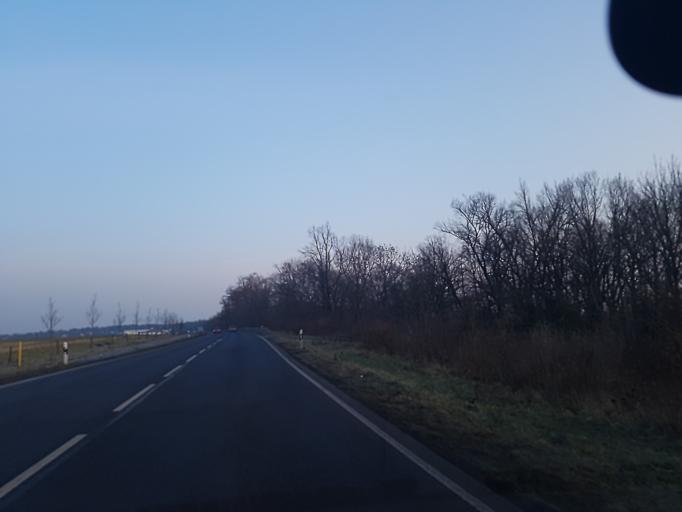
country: DE
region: Saxony-Anhalt
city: Abtsdorf
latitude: 51.8646
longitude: 12.7089
